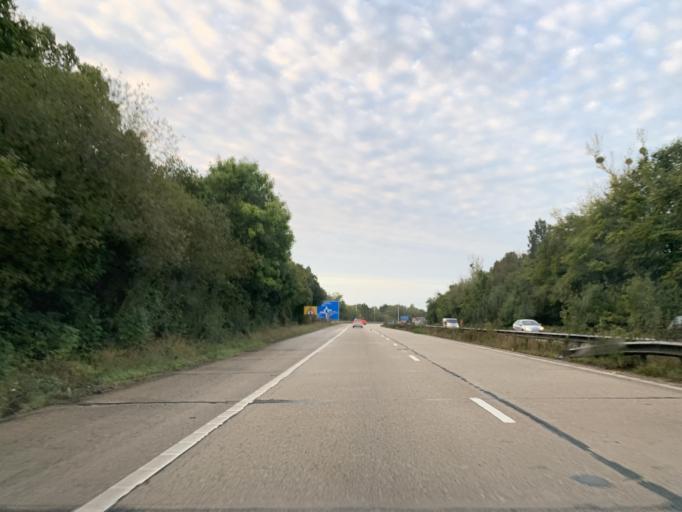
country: GB
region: England
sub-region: Hampshire
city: Totton
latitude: 50.9500
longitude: -1.4753
